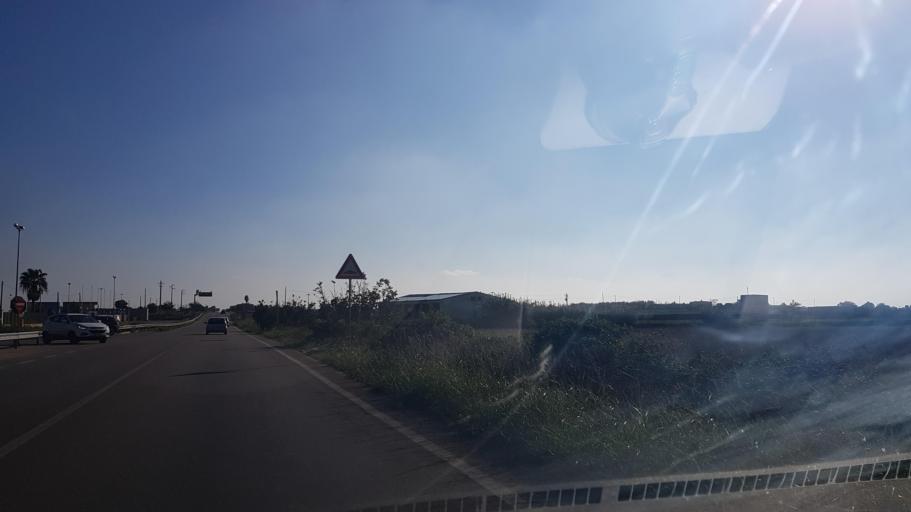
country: IT
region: Apulia
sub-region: Provincia di Lecce
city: Montesano Salentino
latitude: 40.0001
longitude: 18.3233
